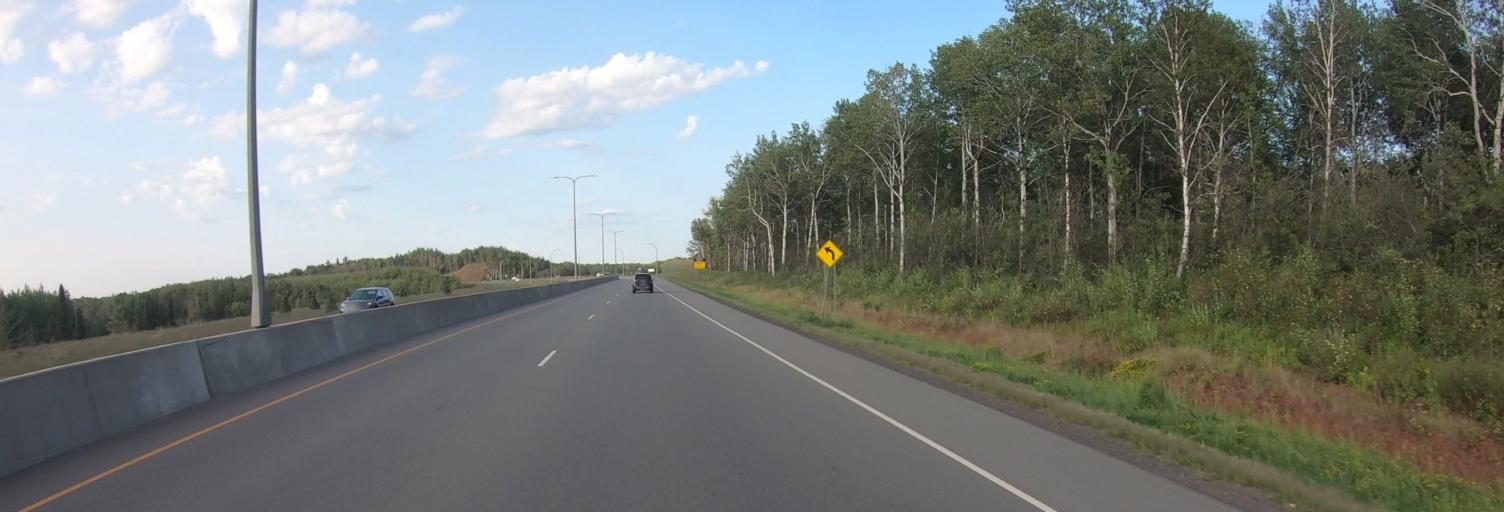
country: US
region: Minnesota
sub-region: Saint Louis County
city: Virginia
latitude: 47.5068
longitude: -92.5145
